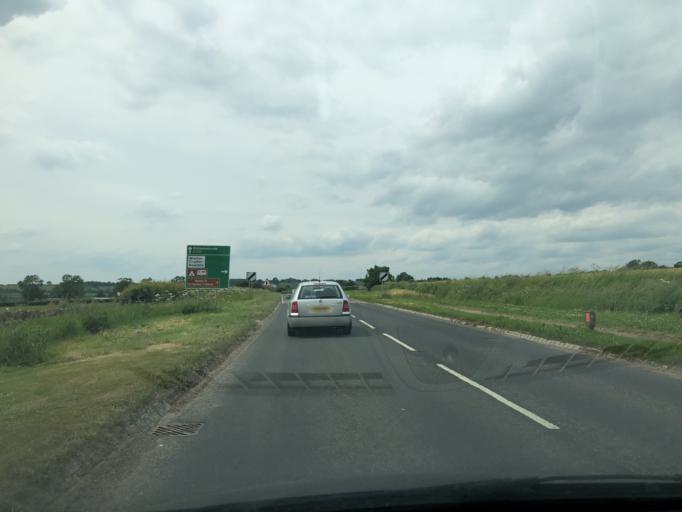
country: GB
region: England
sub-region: North Yorkshire
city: Pickering
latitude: 54.2617
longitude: -0.8132
